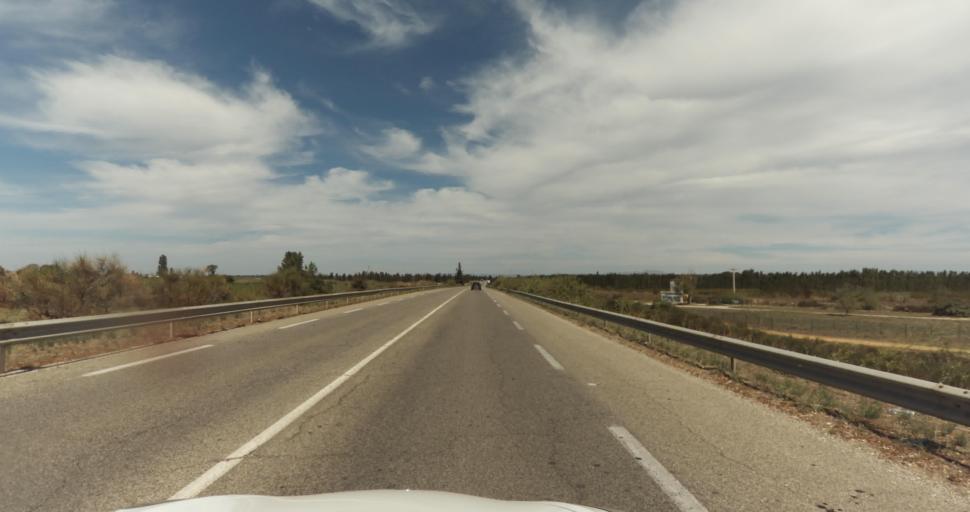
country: FR
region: Provence-Alpes-Cote d'Azur
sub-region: Departement des Bouches-du-Rhone
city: Istres
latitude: 43.5357
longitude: 4.9582
